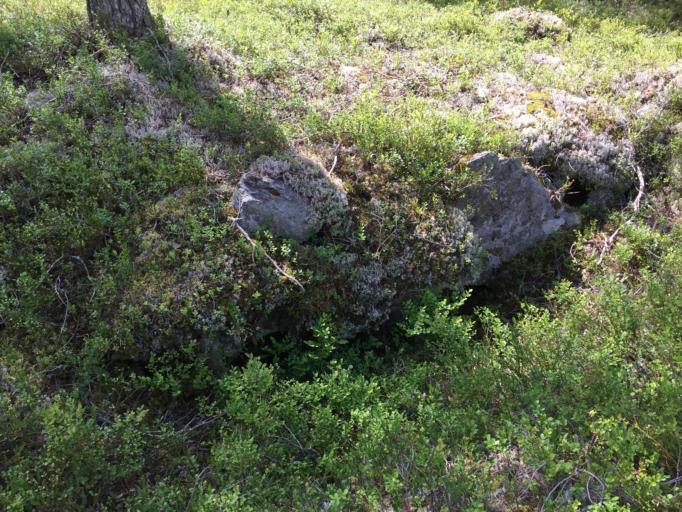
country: SE
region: Dalarna
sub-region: Malung-Saelens kommun
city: Malung
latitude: 60.6459
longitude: 13.7665
